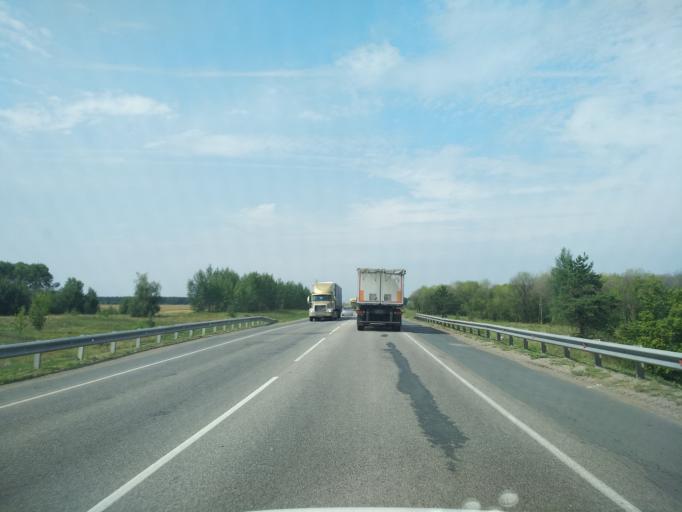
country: RU
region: Voronezj
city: Novaya Usman'
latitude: 51.6996
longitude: 39.4077
